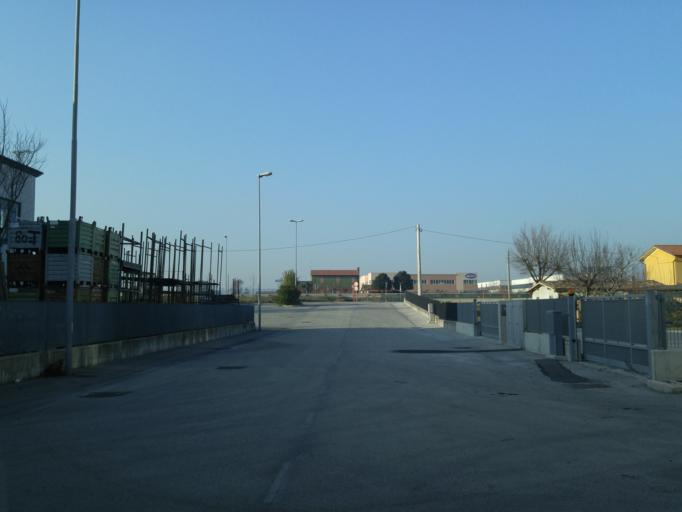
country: IT
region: The Marches
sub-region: Provincia di Pesaro e Urbino
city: Lucrezia
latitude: 43.7674
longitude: 12.9569
